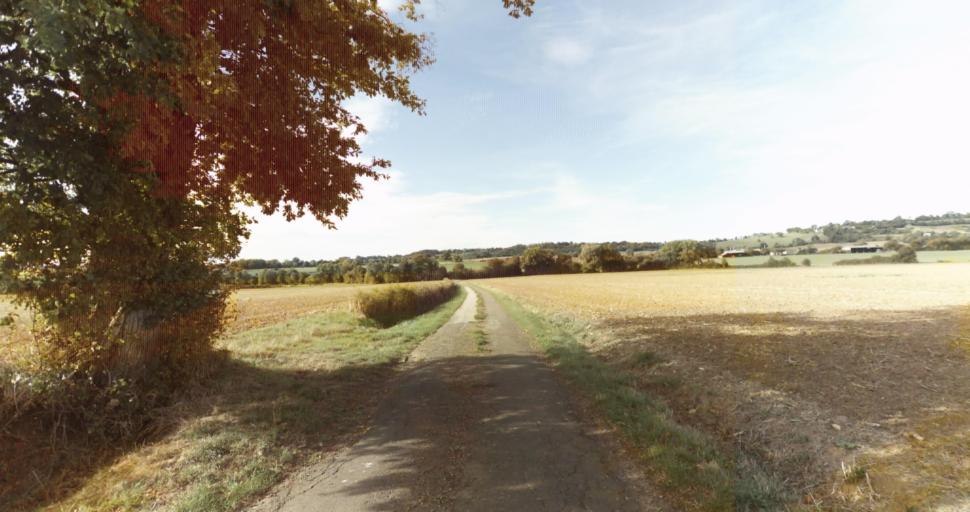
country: FR
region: Lower Normandy
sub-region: Departement de l'Orne
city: Gace
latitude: 48.7176
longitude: 0.2653
